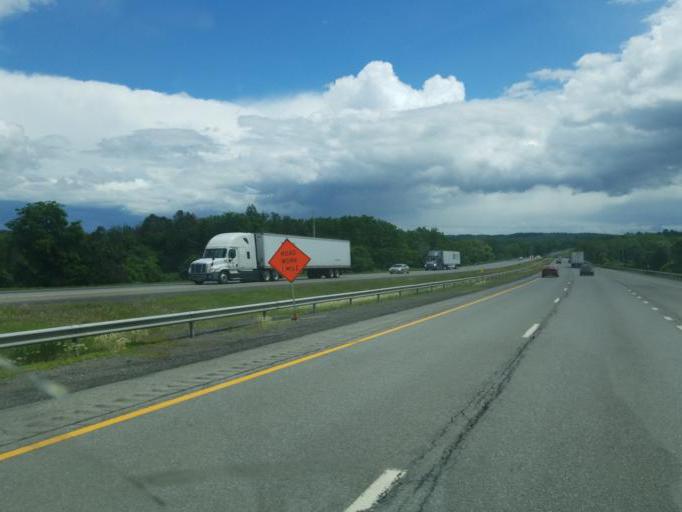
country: US
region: New York
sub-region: Ontario County
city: Victor
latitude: 43.0147
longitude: -77.4759
